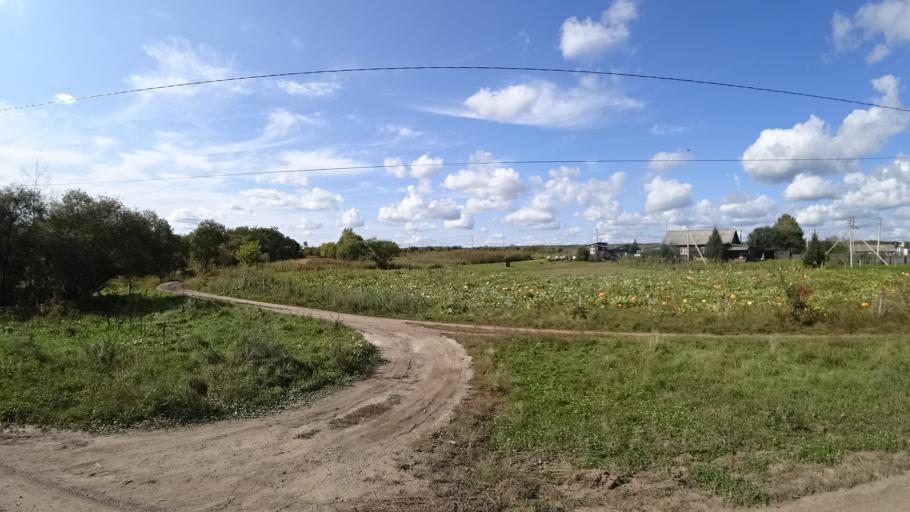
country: RU
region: Amur
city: Arkhara
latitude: 49.4033
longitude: 130.1524
